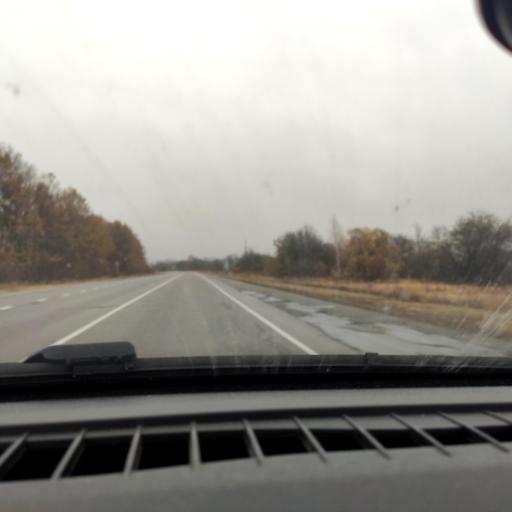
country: RU
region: Voronezj
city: Kolodeznyy
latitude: 51.3220
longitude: 39.0277
